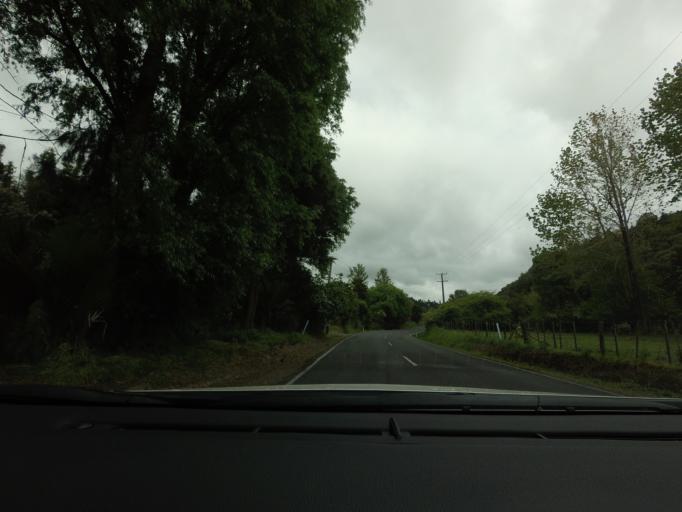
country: NZ
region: Auckland
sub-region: Auckland
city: Warkworth
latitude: -36.5039
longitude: 174.6366
